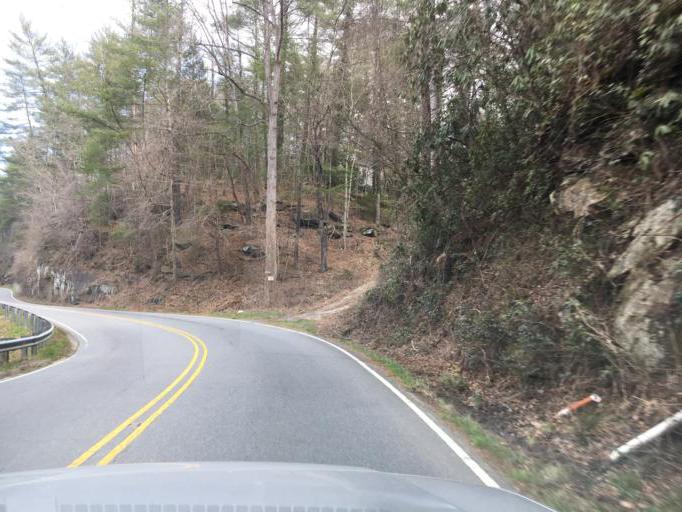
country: US
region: North Carolina
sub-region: Rutherford County
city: Lake Lure
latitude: 35.4209
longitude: -82.1695
